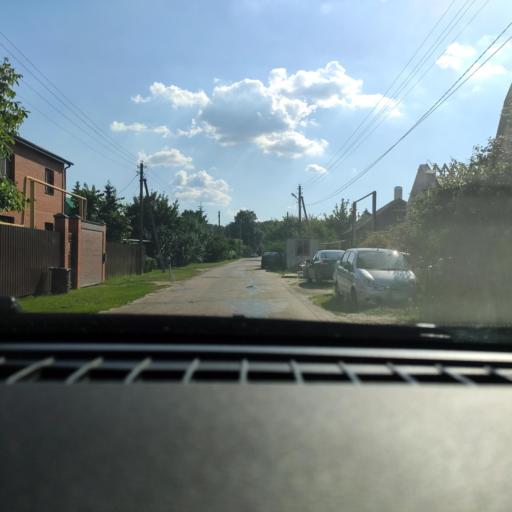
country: RU
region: Voronezj
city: Somovo
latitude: 51.6942
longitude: 39.3208
